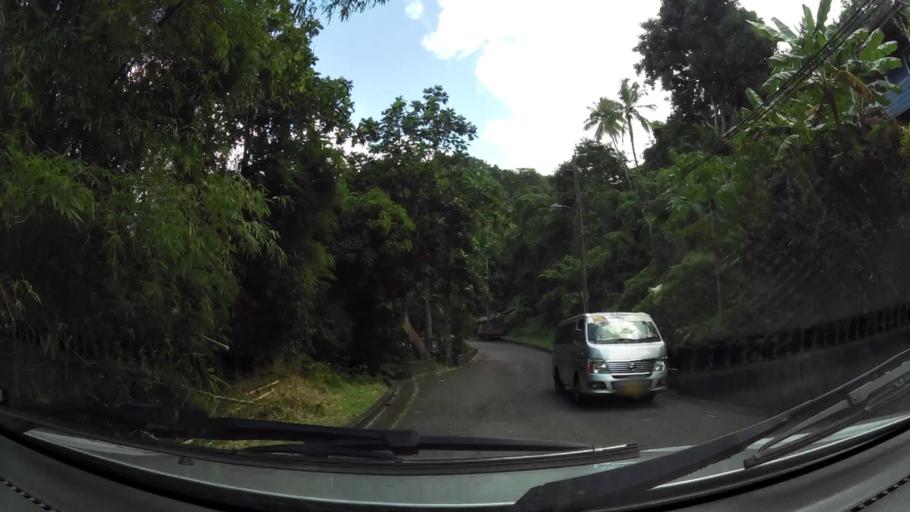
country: GD
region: Saint Mark
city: Victoria
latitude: 12.1852
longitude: -61.7203
